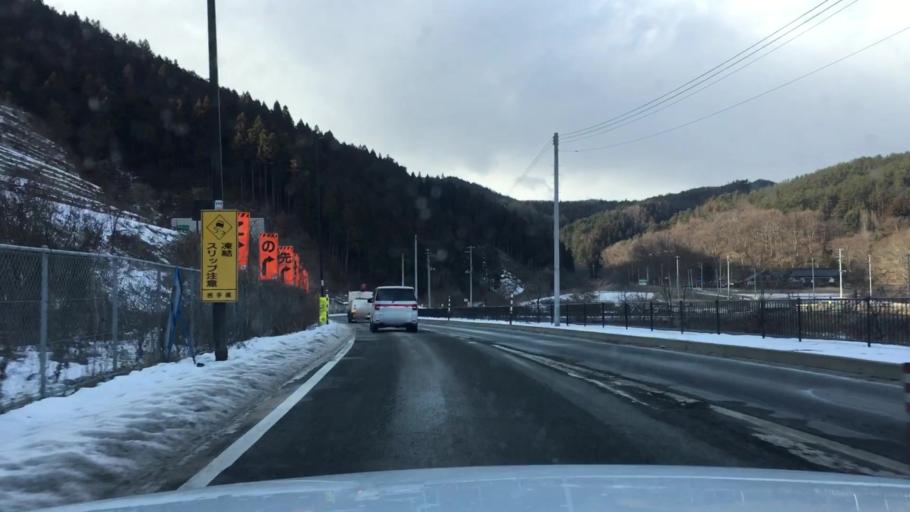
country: JP
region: Iwate
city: Morioka-shi
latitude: 39.6720
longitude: 141.2304
